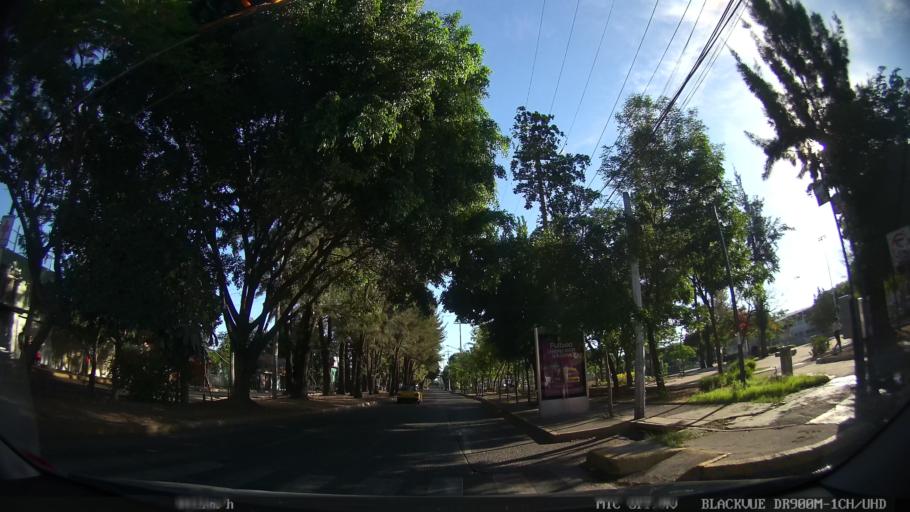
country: MX
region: Jalisco
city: Tlaquepaque
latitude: 20.6612
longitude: -103.2985
